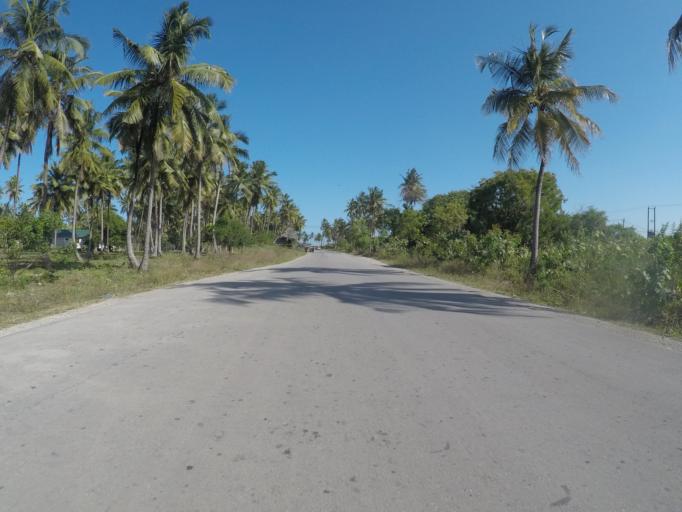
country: TZ
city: Kiwengwa
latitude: -6.1456
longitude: 39.5142
